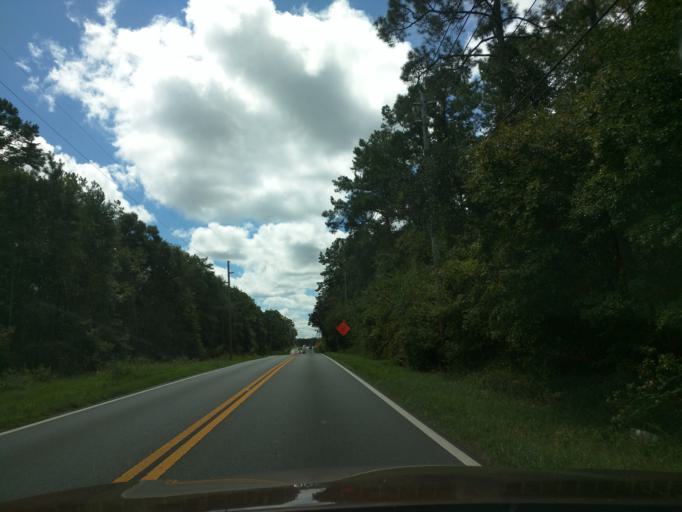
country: US
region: Florida
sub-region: Leon County
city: Tallahassee
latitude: 30.5681
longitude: -84.2239
